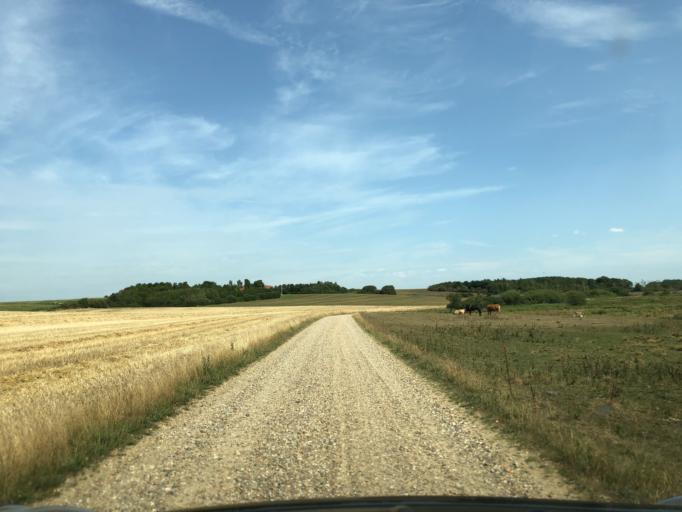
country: DK
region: Central Jutland
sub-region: Ringkobing-Skjern Kommune
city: Skjern
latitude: 55.9969
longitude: 8.4974
